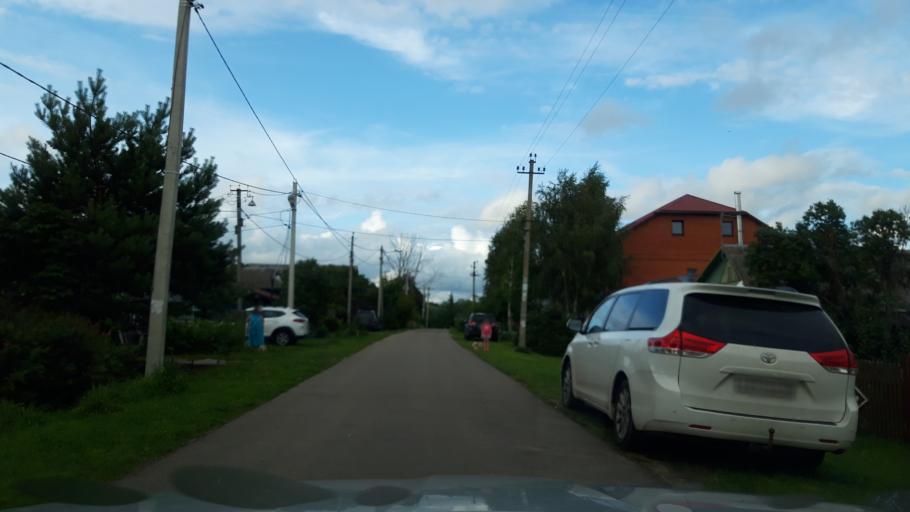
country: RU
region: Moskovskaya
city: Solnechnogorsk
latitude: 56.1039
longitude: 36.8111
